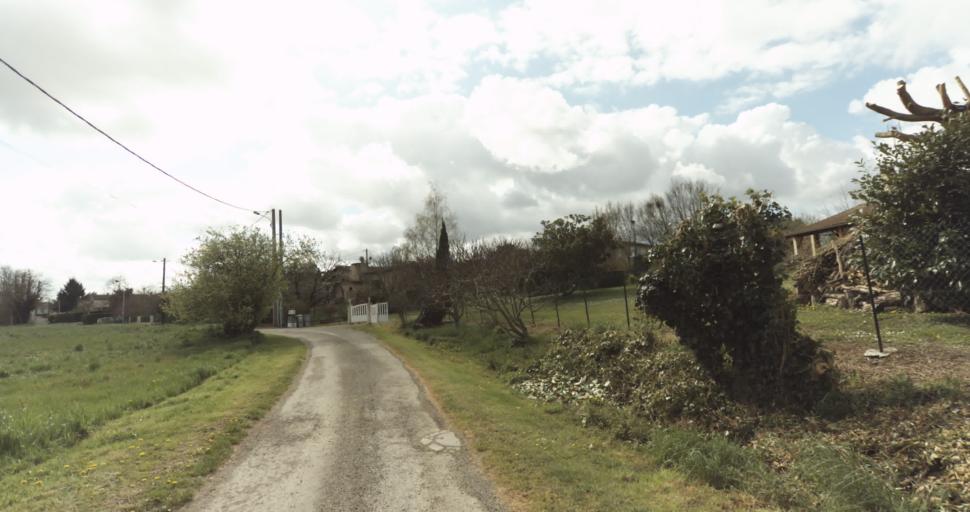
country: FR
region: Midi-Pyrenees
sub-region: Departement de la Haute-Garonne
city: Auterive
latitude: 43.3576
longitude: 1.4690
